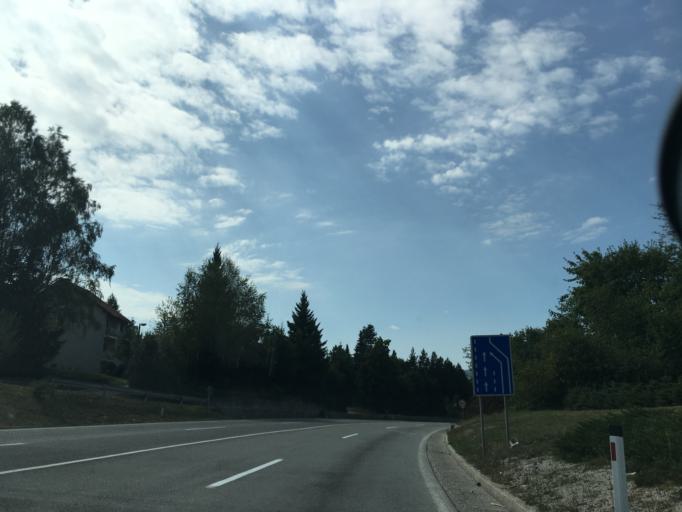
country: RS
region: Central Serbia
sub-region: Zlatiborski Okrug
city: Cajetina
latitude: 43.7355
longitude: 19.7139
